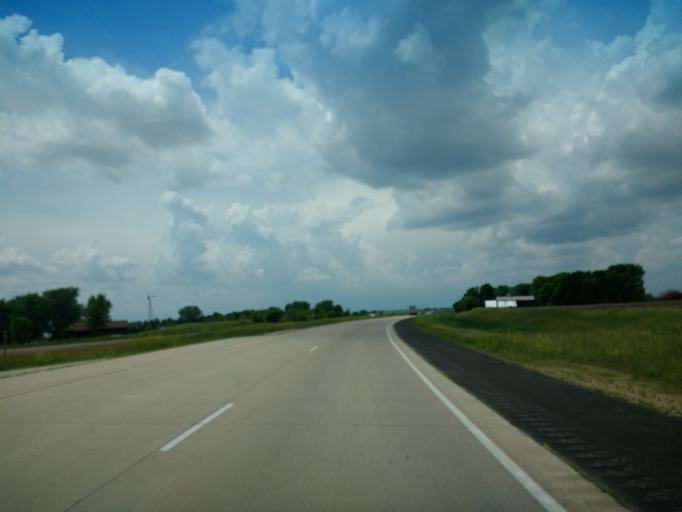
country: US
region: Minnesota
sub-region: Cottonwood County
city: Windom
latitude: 43.8246
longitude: -95.2032
